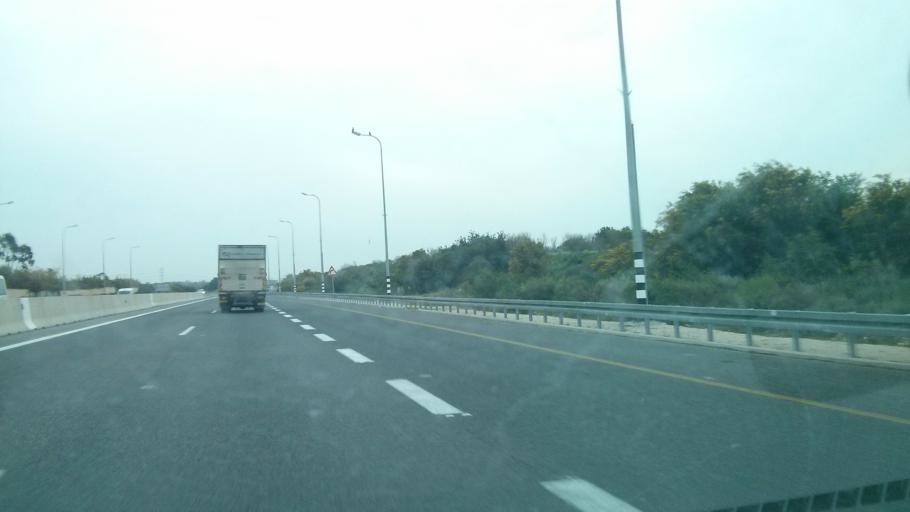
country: IL
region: Haifa
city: Qesarya
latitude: 32.4993
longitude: 34.9164
